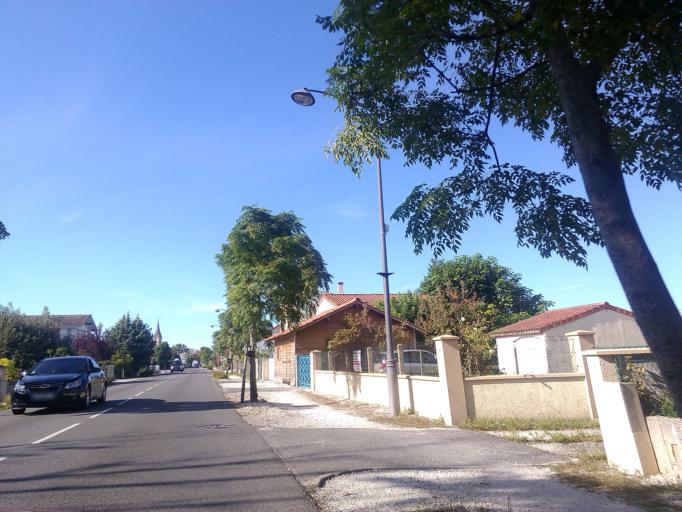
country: FR
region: Aquitaine
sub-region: Departement de la Gironde
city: Hourtin
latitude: 45.1818
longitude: -1.0561
